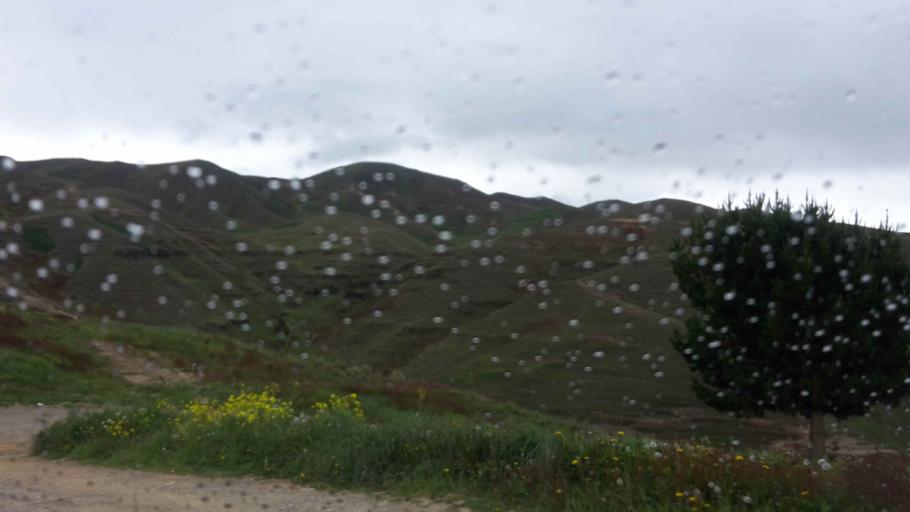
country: BO
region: Cochabamba
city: Cochabamba
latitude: -17.1383
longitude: -66.1070
